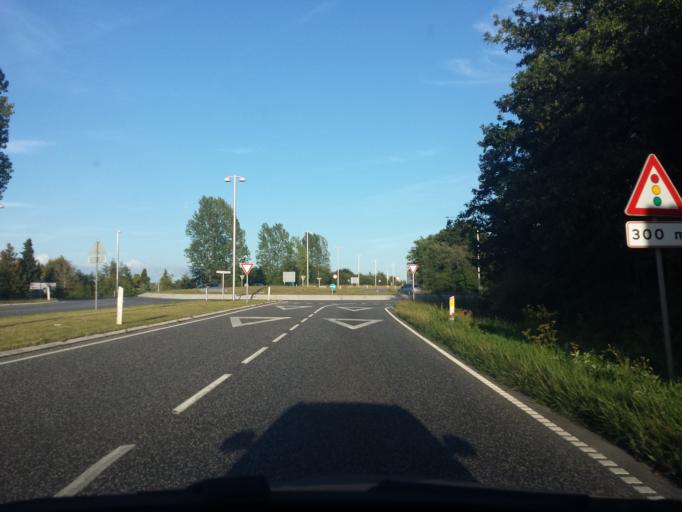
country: DK
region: Capital Region
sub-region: Egedal Kommune
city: Olstykke
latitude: 55.7846
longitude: 12.1509
